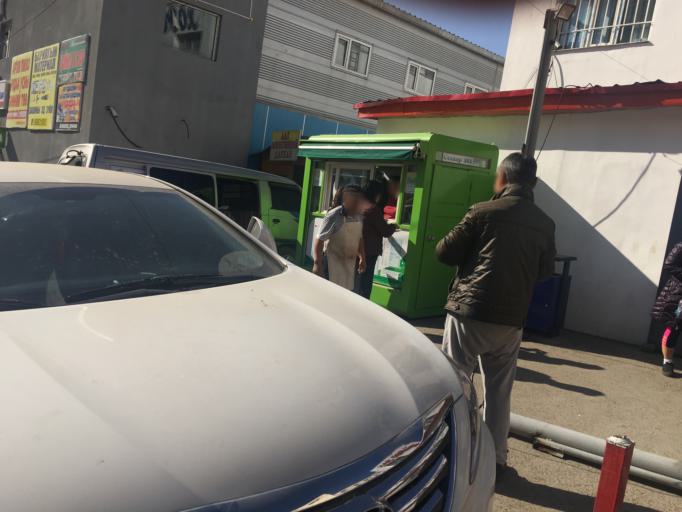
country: MN
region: Ulaanbaatar
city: Ulaanbaatar
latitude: 47.9223
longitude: 106.8815
